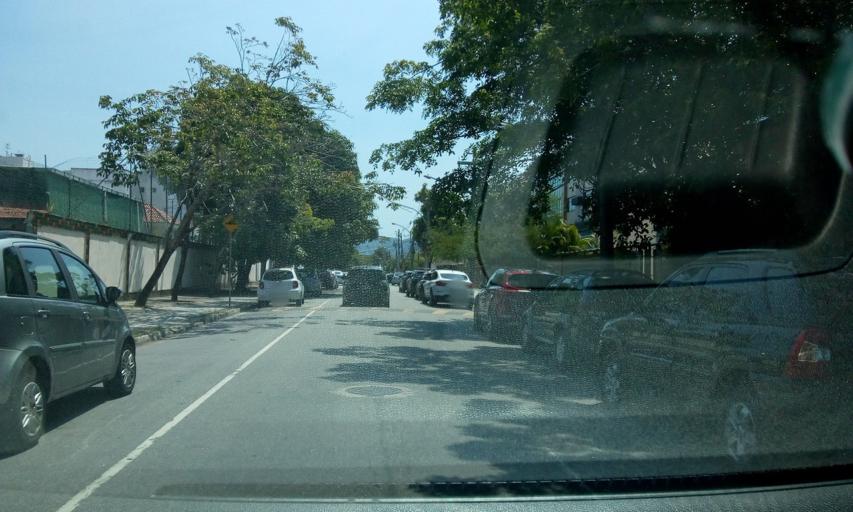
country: BR
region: Rio de Janeiro
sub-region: Nilopolis
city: Nilopolis
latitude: -23.0158
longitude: -43.4684
